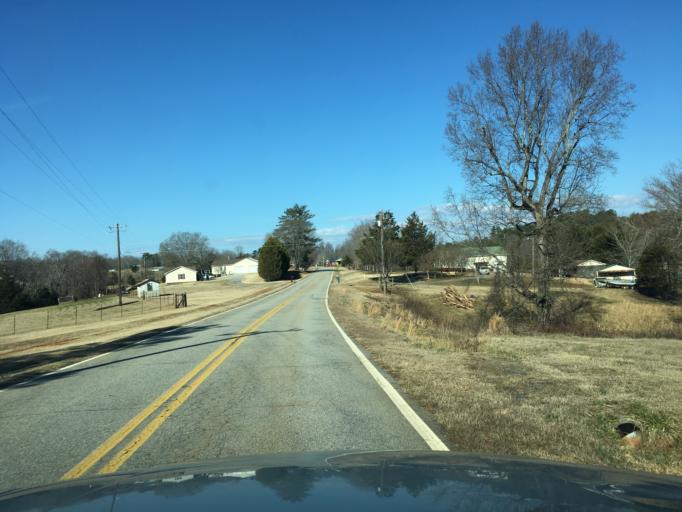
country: US
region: South Carolina
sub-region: Pickens County
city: Pickens
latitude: 34.8565
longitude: -82.7744
